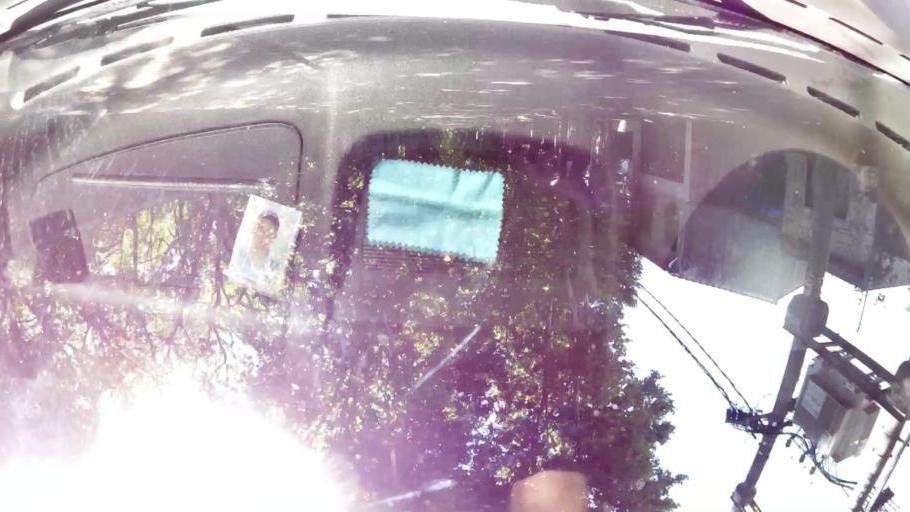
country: AR
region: Buenos Aires
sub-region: Partido de San Isidro
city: San Isidro
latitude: -34.4666
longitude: -58.5252
